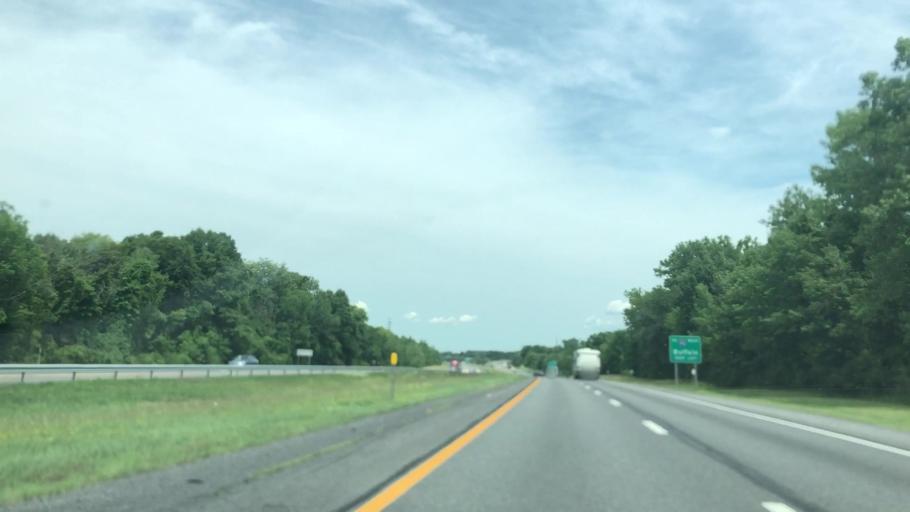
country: US
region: New York
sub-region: Albany County
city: Ravena
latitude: 42.5043
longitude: -73.7930
